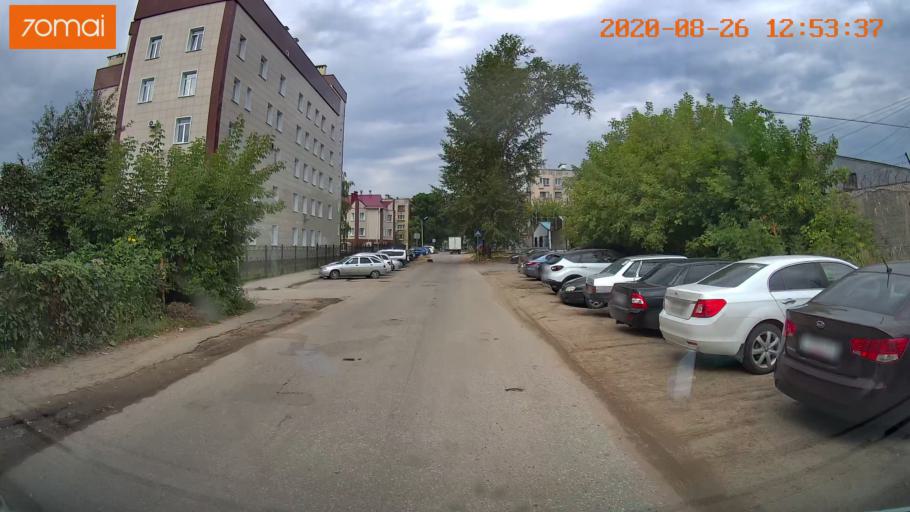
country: RU
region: Rjazan
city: Ryazan'
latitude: 54.6015
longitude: 39.7599
